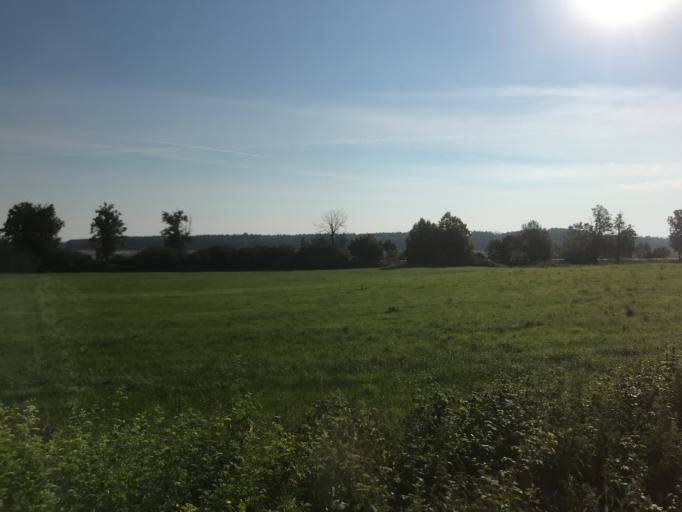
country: CZ
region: Jihocesky
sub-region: Okres Jindrichuv Hradec
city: Lomnice nad Luznici
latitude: 49.0725
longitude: 14.7309
